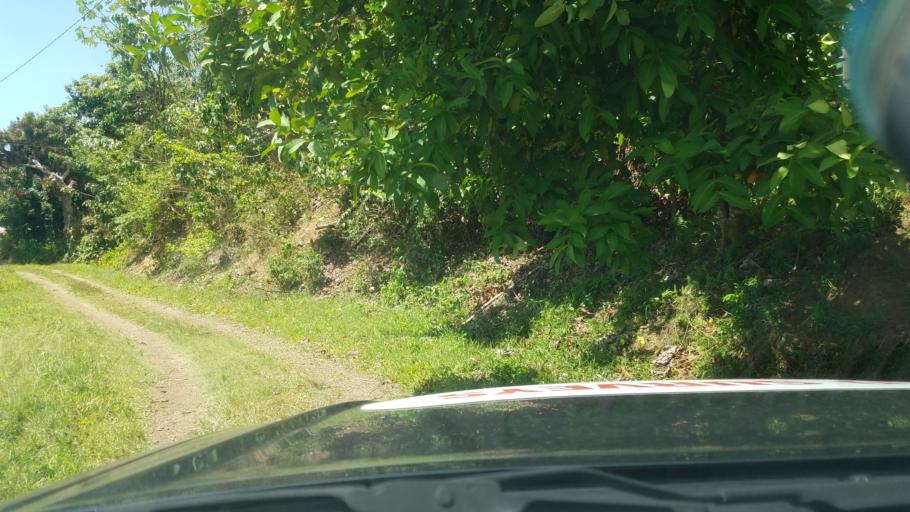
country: LC
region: Castries Quarter
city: Bisee
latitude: 14.0279
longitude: -60.9527
